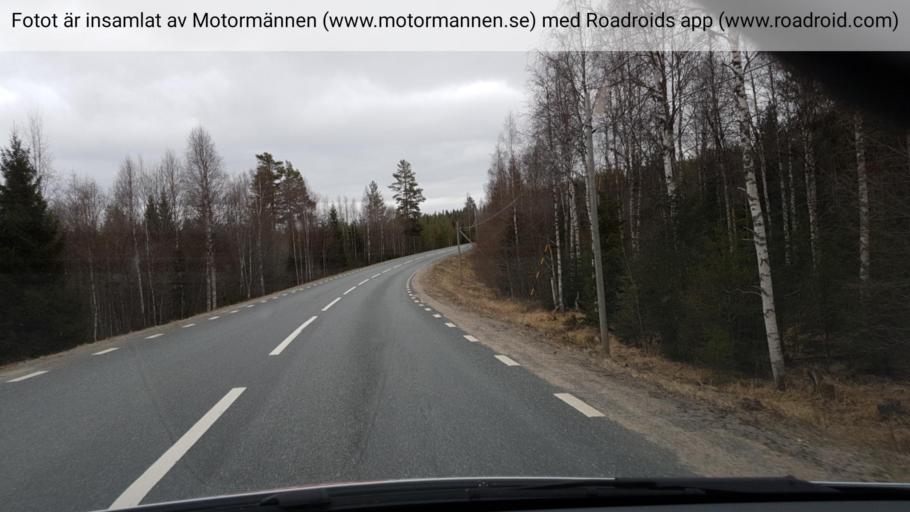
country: SE
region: Vaesternorrland
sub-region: OErnskoeldsviks Kommun
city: Ornskoldsvik
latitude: 63.6803
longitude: 18.5298
